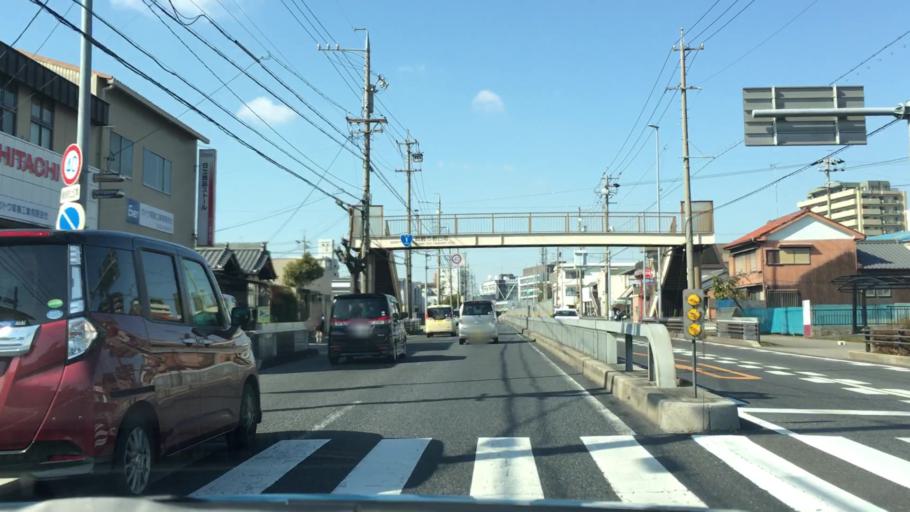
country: JP
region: Aichi
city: Okazaki
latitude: 34.9514
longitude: 137.1791
